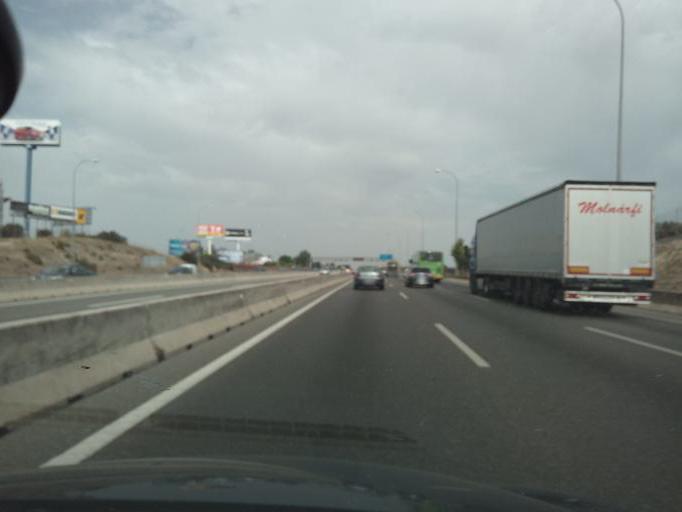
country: ES
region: Madrid
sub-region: Provincia de Madrid
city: Majadahonda
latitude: 40.4784
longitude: -3.8455
